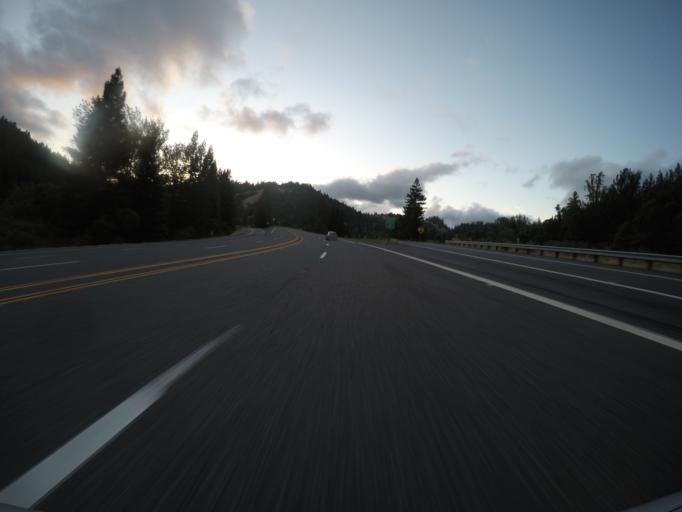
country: US
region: California
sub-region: Humboldt County
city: Redway
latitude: 40.0638
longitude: -123.7840
